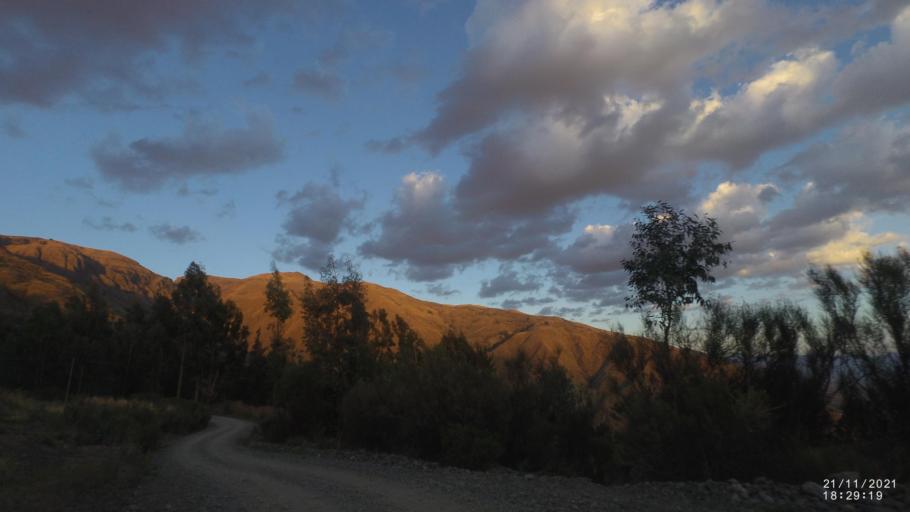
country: BO
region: Cochabamba
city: Cochabamba
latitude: -17.3088
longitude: -66.2161
